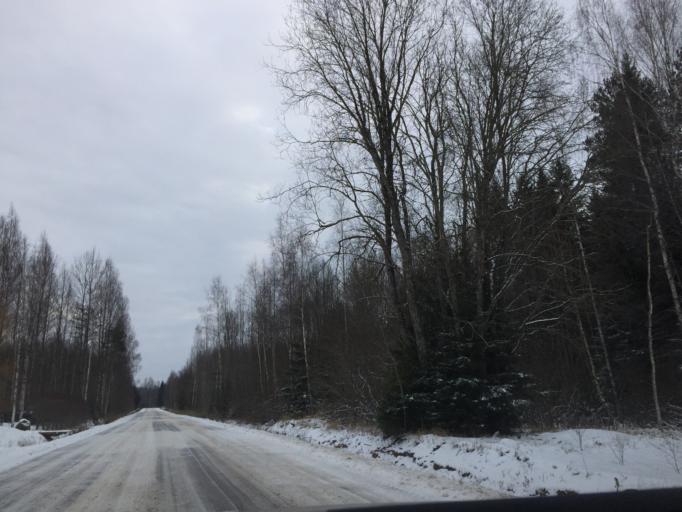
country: LV
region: Amatas Novads
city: Drabesi
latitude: 57.2152
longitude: 25.1688
